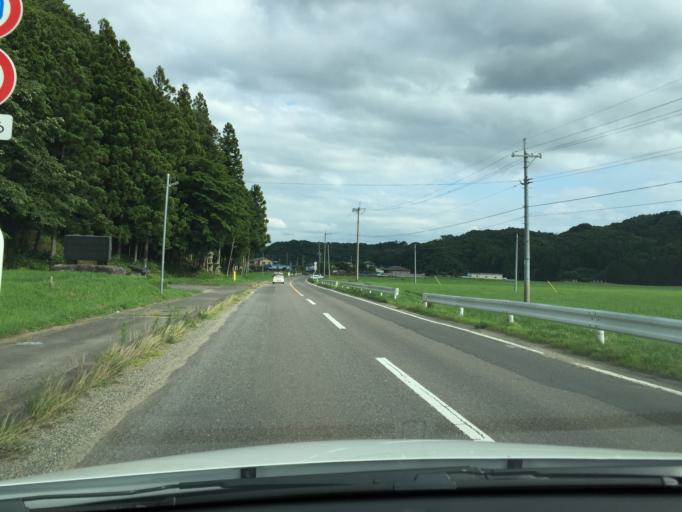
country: JP
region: Tochigi
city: Kuroiso
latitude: 37.1791
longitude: 140.1495
